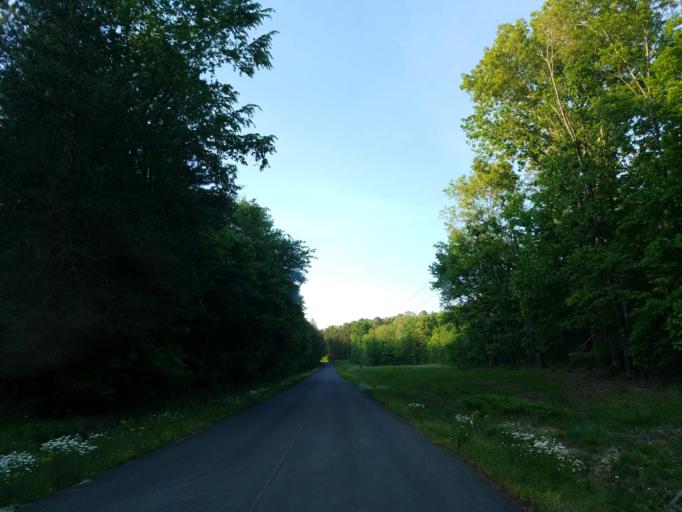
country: US
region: Georgia
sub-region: Whitfield County
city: Dalton
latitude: 34.6514
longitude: -85.0834
